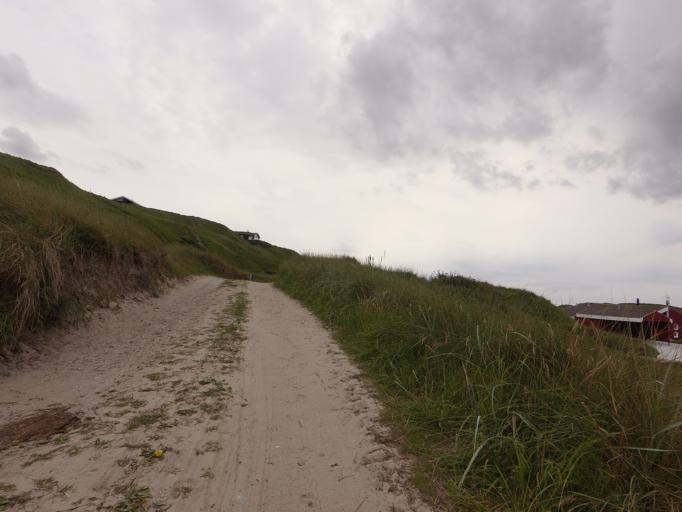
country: DK
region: North Denmark
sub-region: Jammerbugt Kommune
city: Pandrup
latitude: 57.3081
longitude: 9.6469
